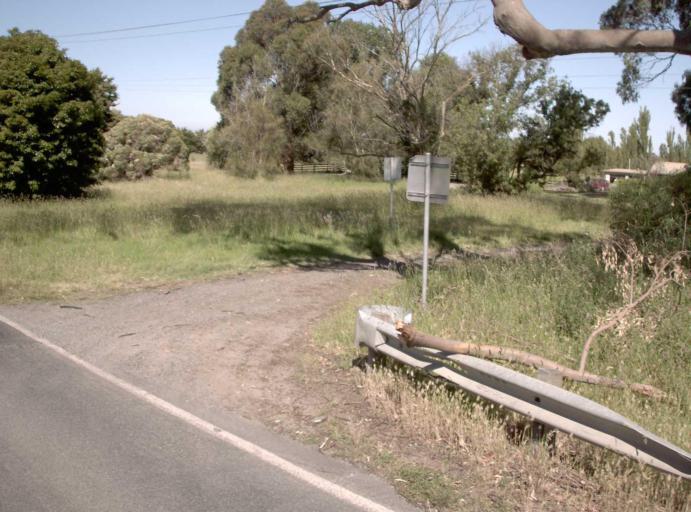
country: AU
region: Victoria
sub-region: Latrobe
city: Morwell
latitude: -38.6438
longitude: 146.4813
